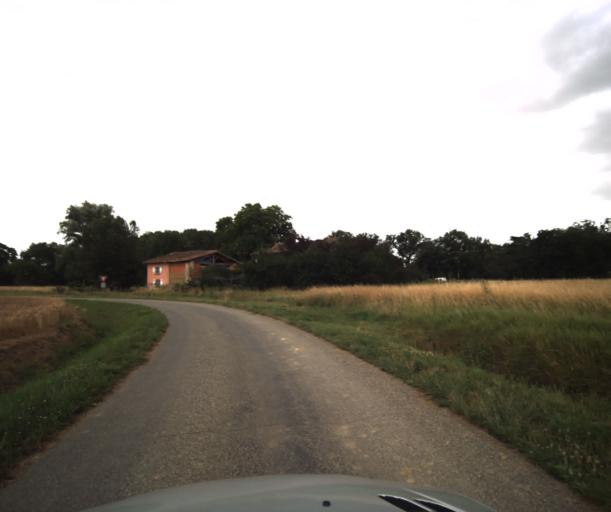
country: FR
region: Midi-Pyrenees
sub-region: Departement de la Haute-Garonne
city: Labarthe-sur-Leze
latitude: 43.4680
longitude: 1.4088
